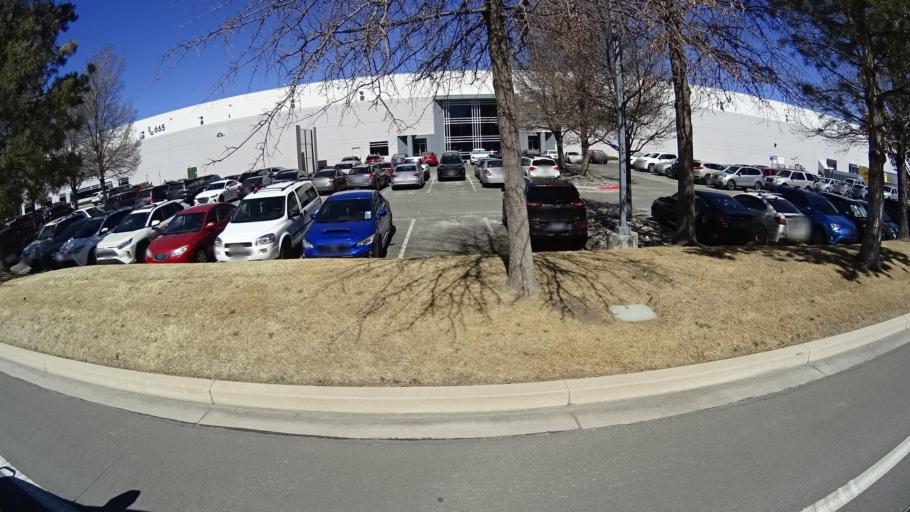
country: US
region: Nevada
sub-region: Washoe County
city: Sparks
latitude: 39.4613
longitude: -119.7707
